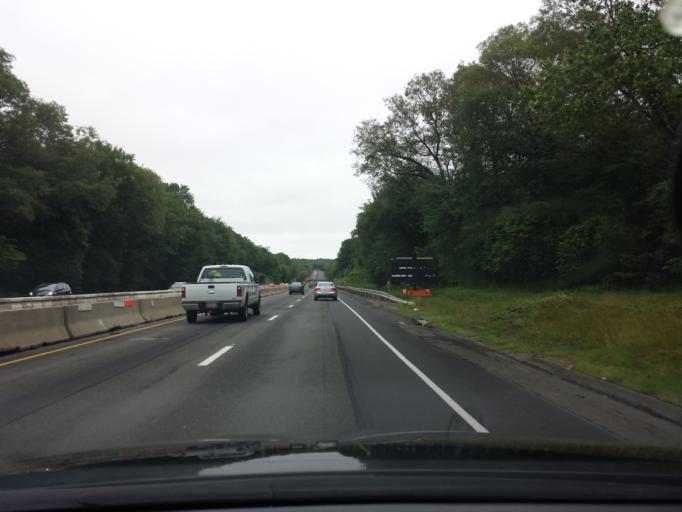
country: US
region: Connecticut
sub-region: Middlesex County
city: Old Saybrook Center
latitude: 41.3203
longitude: -72.3113
